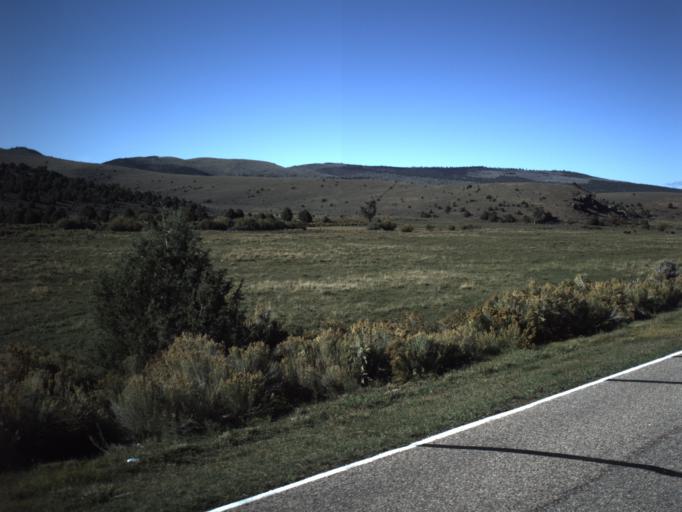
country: US
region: Utah
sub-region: Garfield County
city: Panguitch
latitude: 37.7577
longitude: -112.5609
